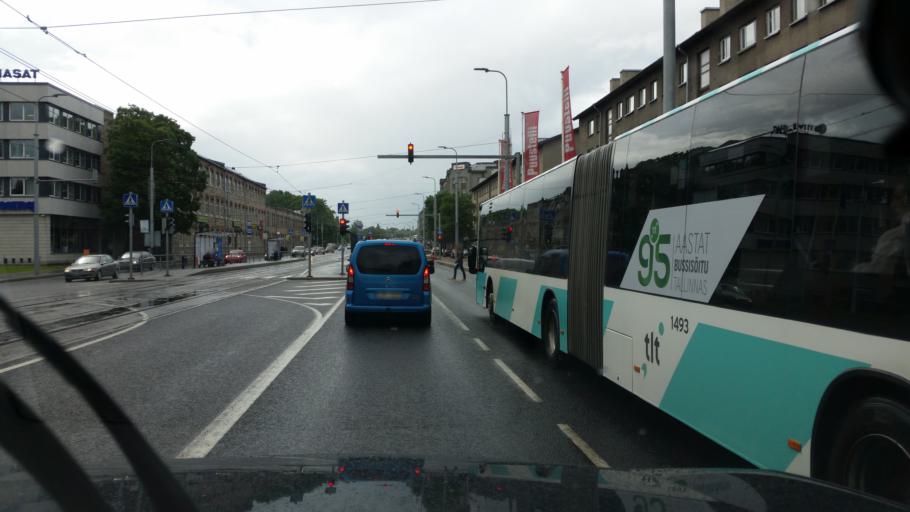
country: EE
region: Harju
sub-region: Tallinna linn
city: Tallinn
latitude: 59.4253
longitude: 24.7425
